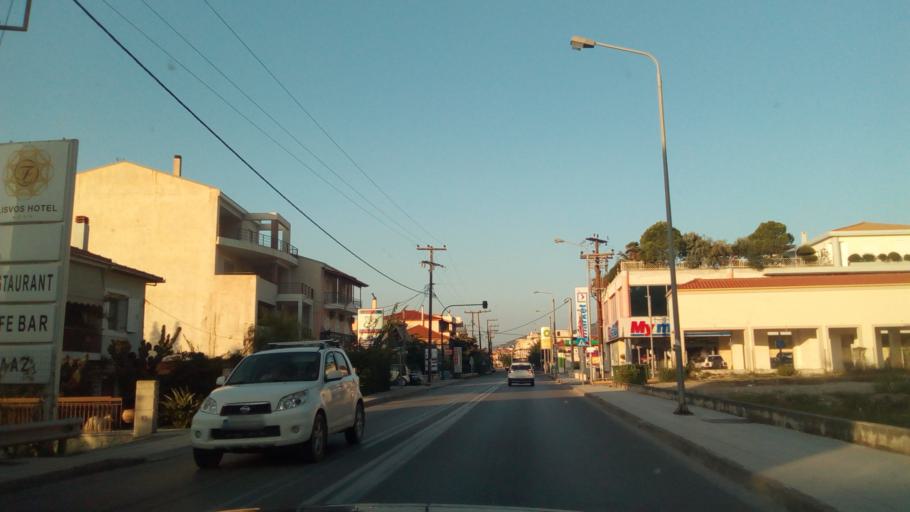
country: GR
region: West Greece
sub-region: Nomos Aitolias kai Akarnanias
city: Nafpaktos
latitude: 38.3901
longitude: 21.8200
